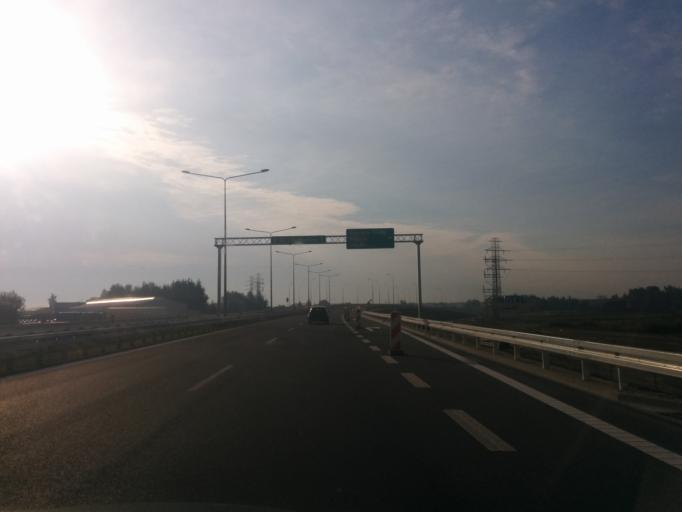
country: PL
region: Masovian Voivodeship
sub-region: Powiat pruszkowski
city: Nowe Grocholice
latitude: 52.1178
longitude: 20.8858
